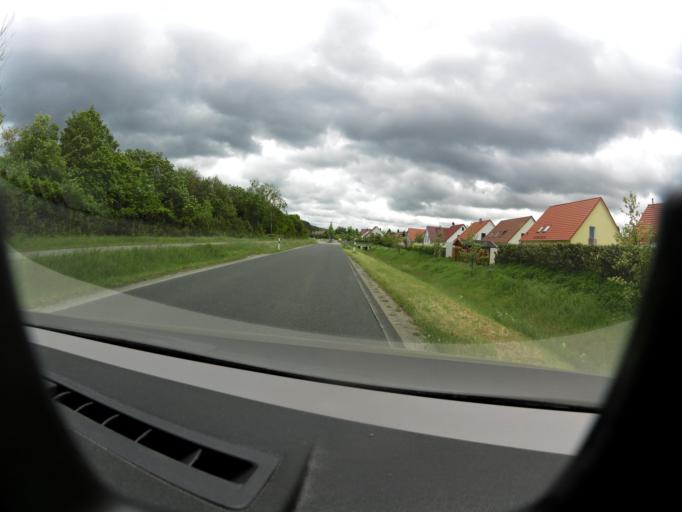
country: DE
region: Bavaria
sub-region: Regierungsbezirk Unterfranken
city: Iphofen
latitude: 49.7109
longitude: 10.2534
